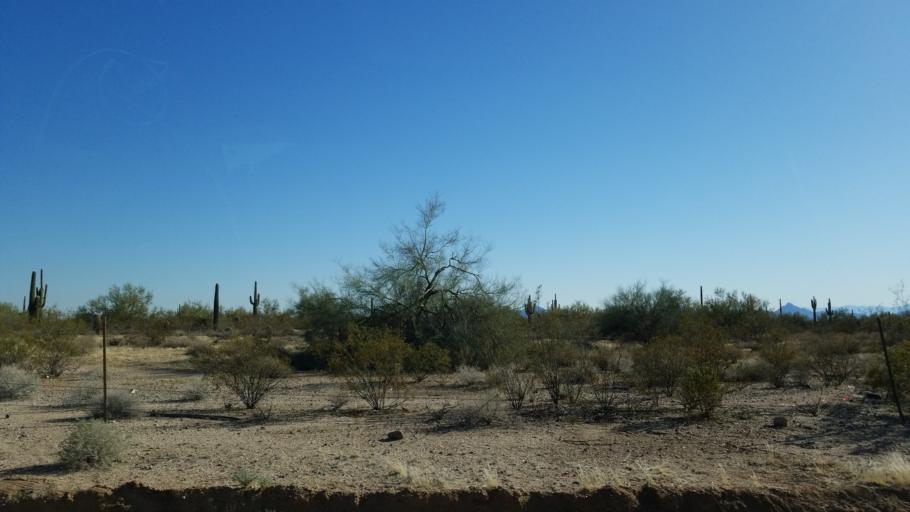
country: US
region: Arizona
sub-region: Maricopa County
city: Carefree
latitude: 33.6987
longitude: -111.9473
